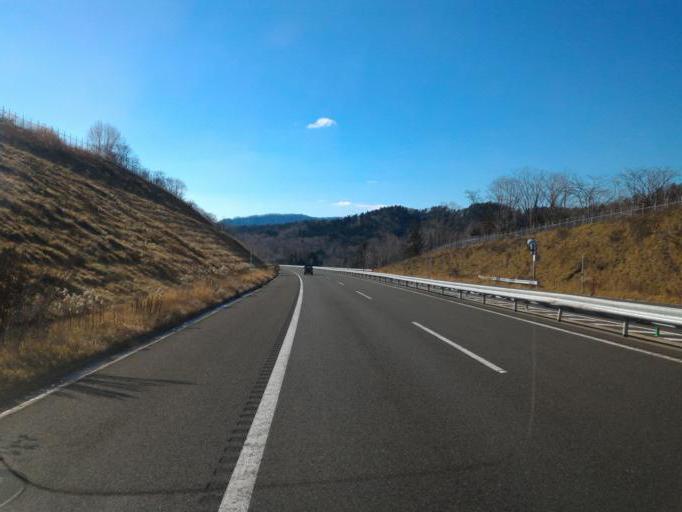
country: JP
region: Hokkaido
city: Shimo-furano
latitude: 42.9399
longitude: 142.2125
